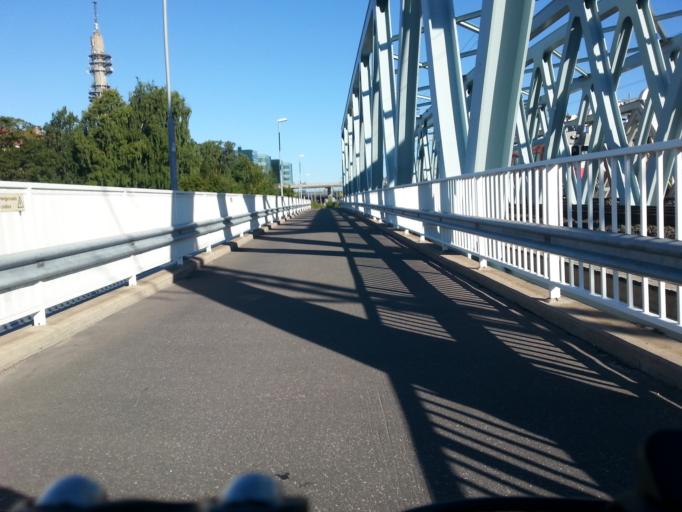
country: FI
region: Uusimaa
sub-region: Helsinki
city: Helsinki
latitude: 60.2029
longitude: 24.9303
